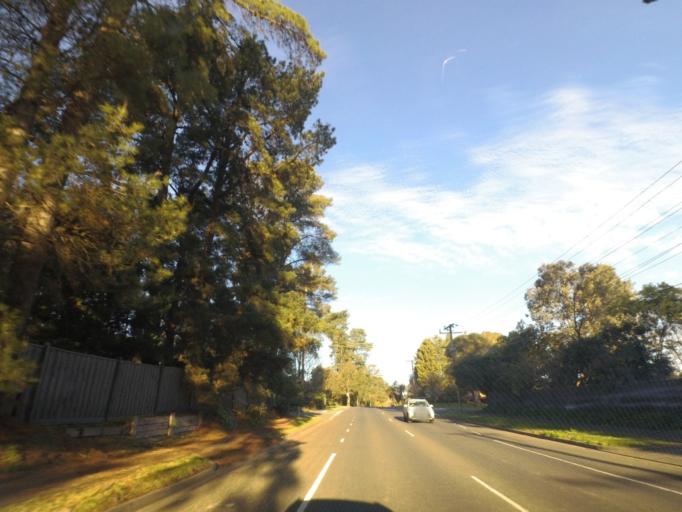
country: AU
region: Victoria
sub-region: Manningham
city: Park Orchards
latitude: -37.7805
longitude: 145.2228
